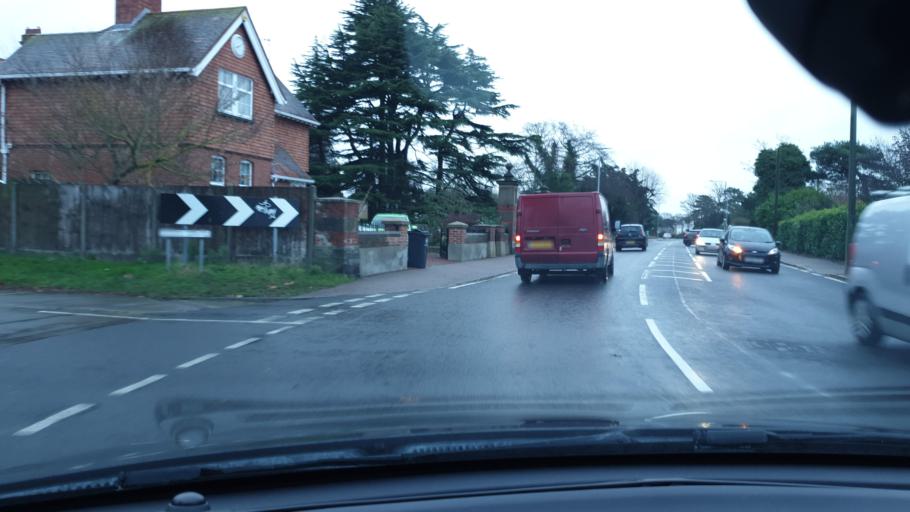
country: GB
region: England
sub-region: Essex
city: Clacton-on-Sea
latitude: 51.7960
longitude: 1.1645
